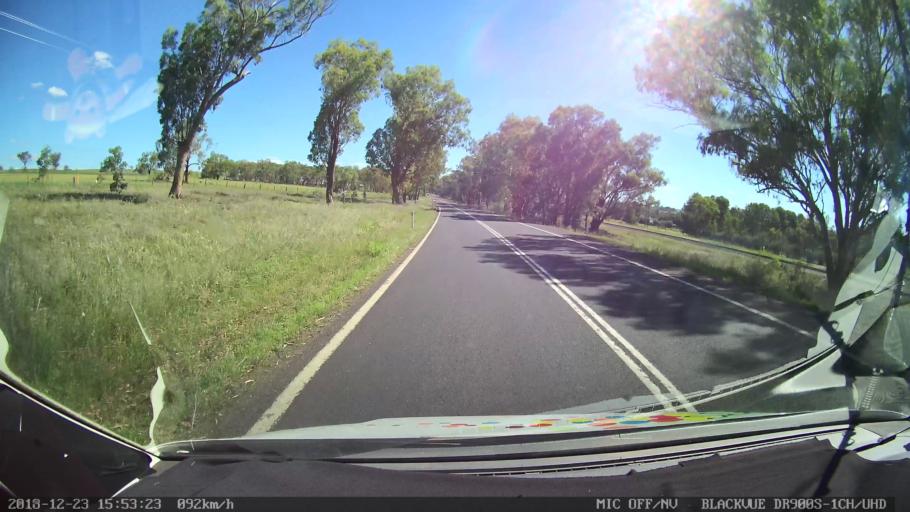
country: AU
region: New South Wales
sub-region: Tamworth Municipality
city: Phillip
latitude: -31.1323
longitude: 150.8813
